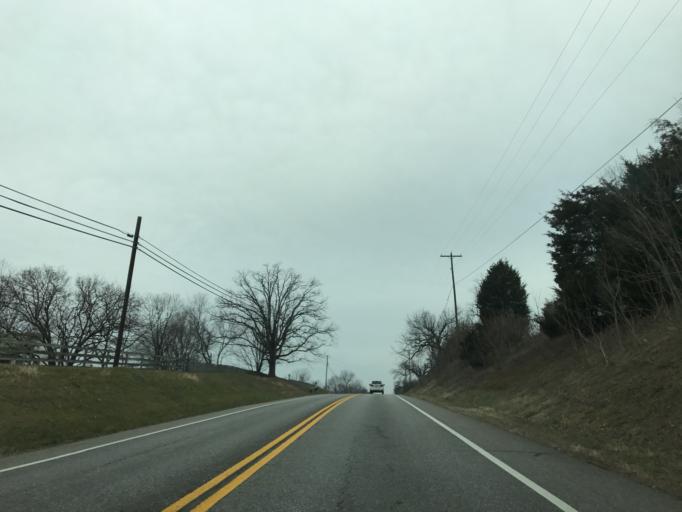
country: US
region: Maryland
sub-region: Frederick County
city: Emmitsburg
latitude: 39.7091
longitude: -77.3366
